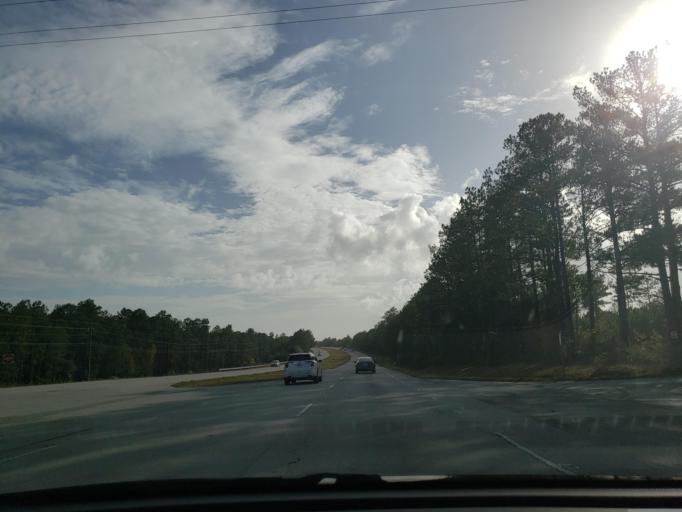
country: US
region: North Carolina
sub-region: Onslow County
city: Sneads Ferry
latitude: 34.6218
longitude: -77.4835
